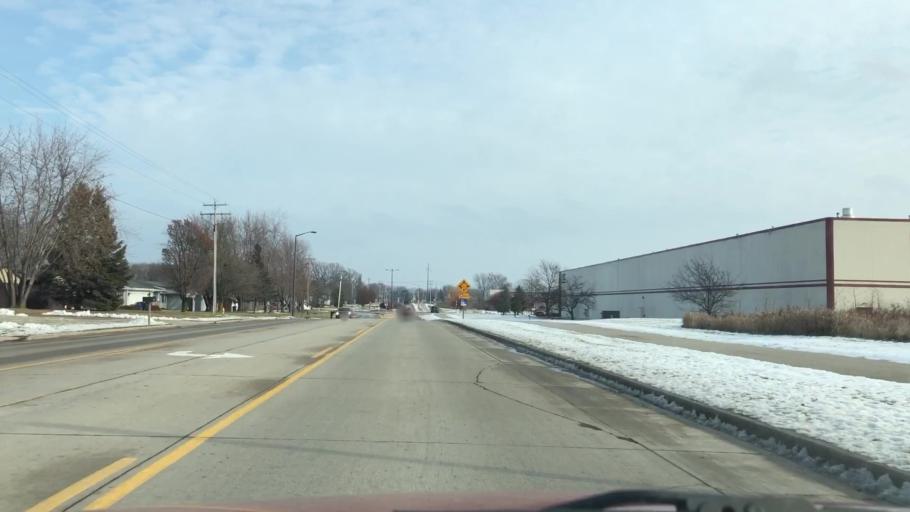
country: US
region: Wisconsin
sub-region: Brown County
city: De Pere
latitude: 44.4306
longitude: -88.0889
